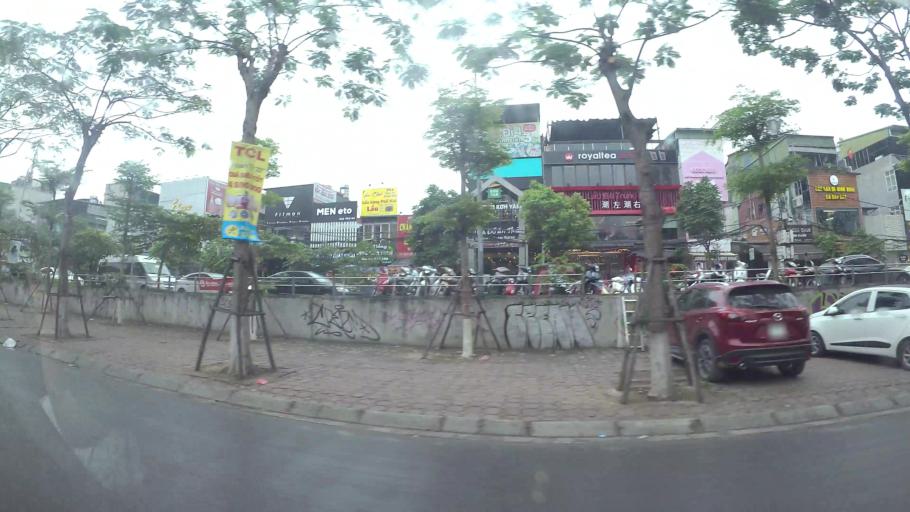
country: VN
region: Ha Noi
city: Dong Da
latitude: 21.0156
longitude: 105.8169
